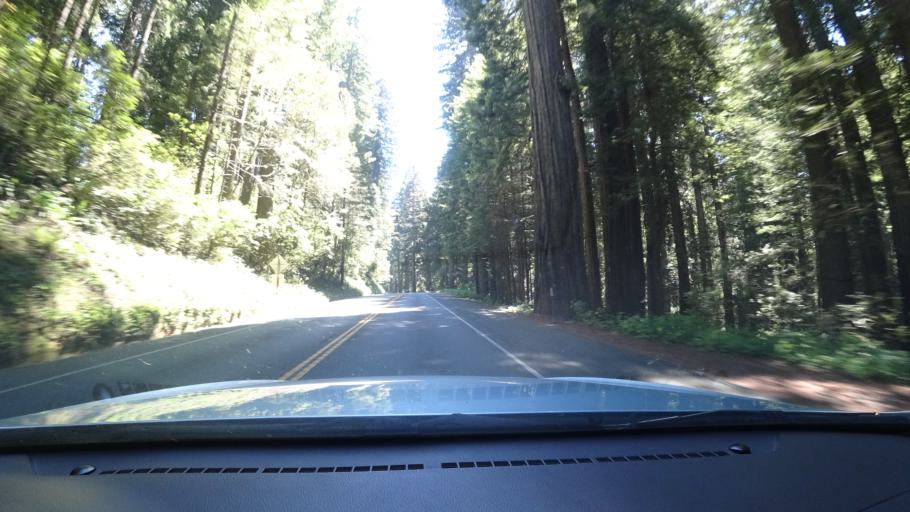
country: US
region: California
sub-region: Del Norte County
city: Bertsch-Oceanview
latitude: 41.6542
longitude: -124.1175
